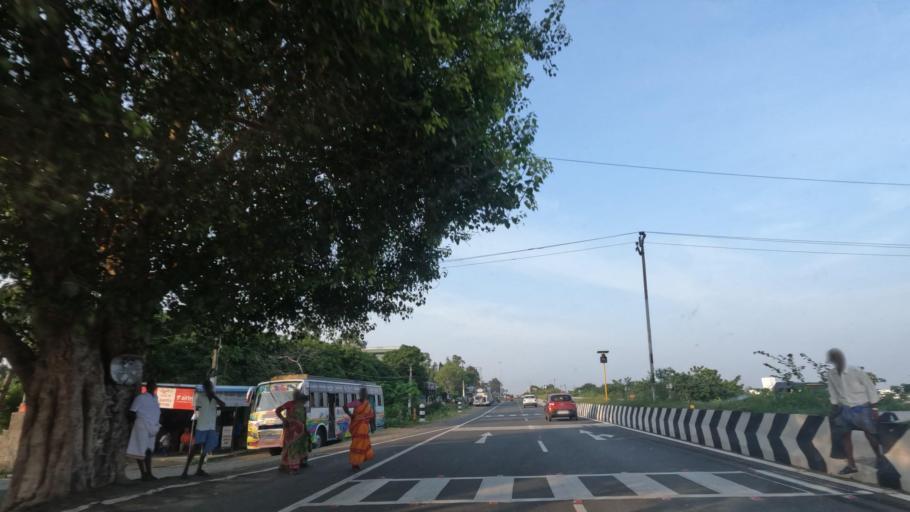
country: IN
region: Tamil Nadu
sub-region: Kancheepuram
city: Mamallapuram
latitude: 12.6891
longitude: 80.2171
